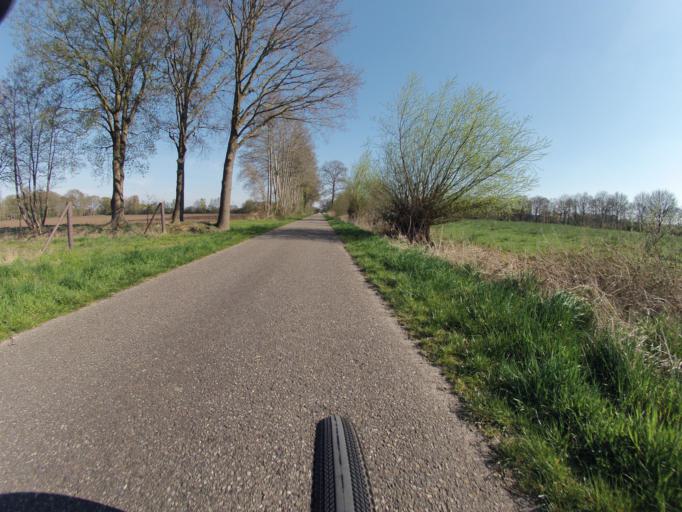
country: DE
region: Lower Saxony
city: Isterberg
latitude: 52.3508
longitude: 7.1640
